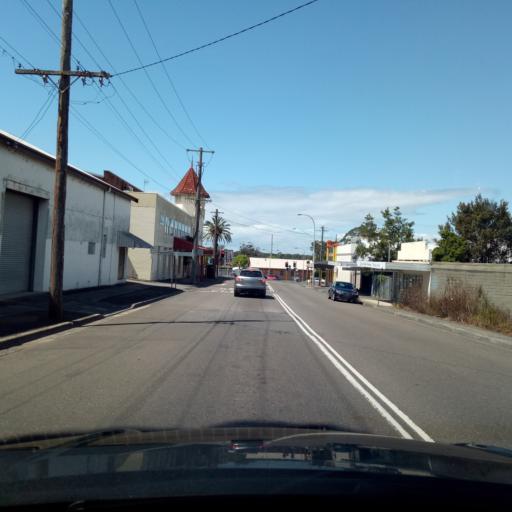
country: AU
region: New South Wales
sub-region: Wyong Shire
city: Chittaway Bay
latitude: -33.2855
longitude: 151.4236
